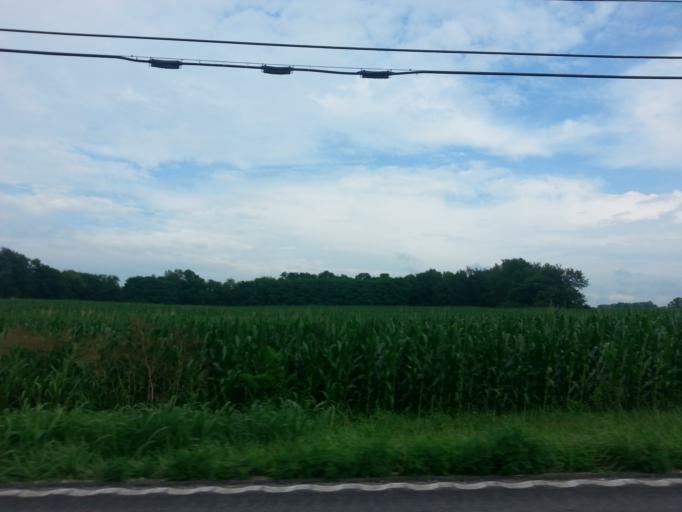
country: US
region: Kentucky
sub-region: Harrison County
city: Cynthiana
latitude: 38.4082
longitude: -84.2693
